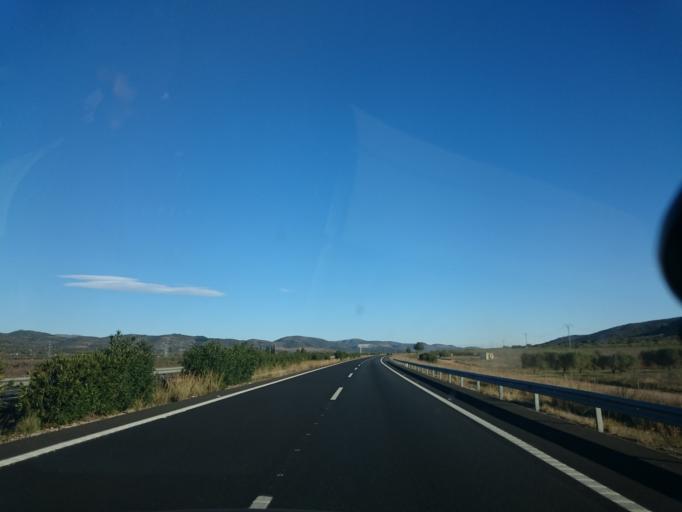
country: ES
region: Valencia
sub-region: Provincia de Castello
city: Alcala de Xivert
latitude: 40.3059
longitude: 0.2391
